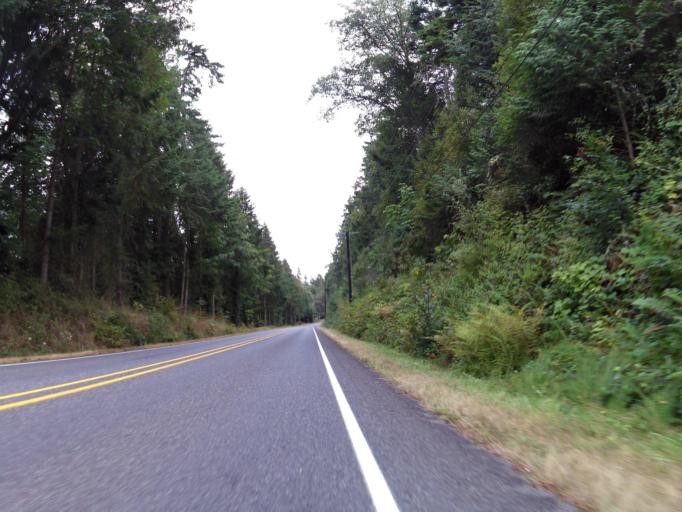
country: US
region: Washington
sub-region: Jefferson County
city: Port Hadlock-Irondale
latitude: 48.0072
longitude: -122.7268
